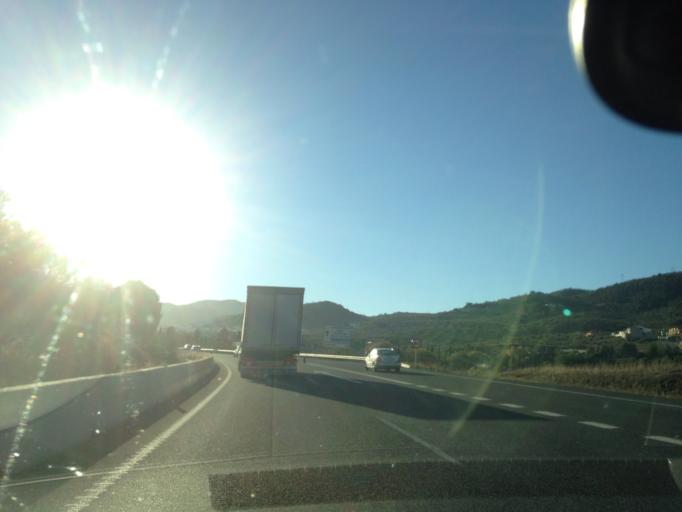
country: ES
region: Andalusia
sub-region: Provincia de Malaga
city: Casabermeja
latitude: 36.9054
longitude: -4.4454
